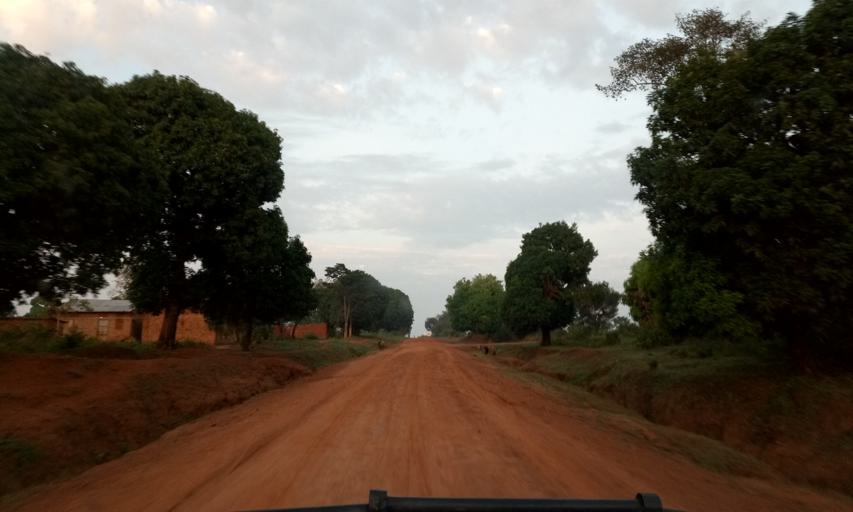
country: UG
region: Eastern Region
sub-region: Ngora District
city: Ngora
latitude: 1.4667
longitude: 33.8067
